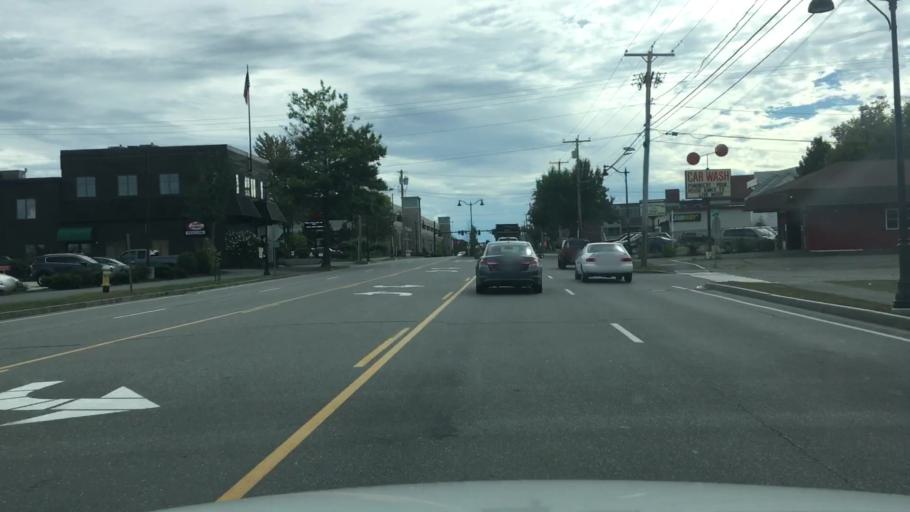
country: US
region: Maine
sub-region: Penobscot County
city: Bangor
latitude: 44.7913
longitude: -68.7766
